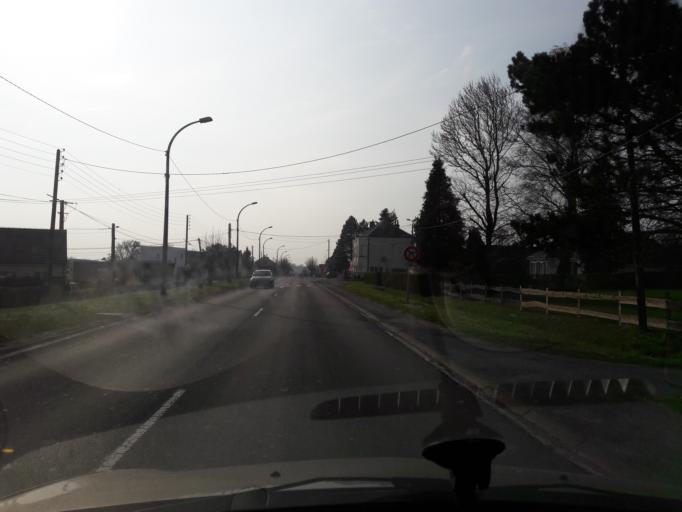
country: FR
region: Nord-Pas-de-Calais
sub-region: Departement du Nord
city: Rousies
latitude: 50.2602
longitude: 4.0107
